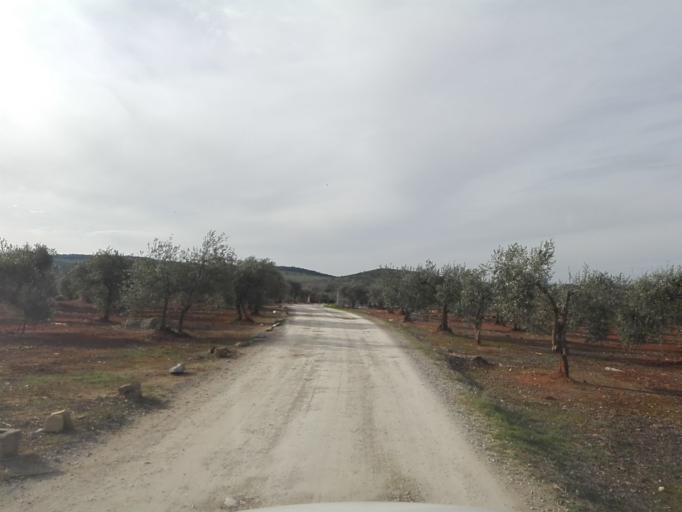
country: ES
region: Extremadura
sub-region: Provincia de Badajoz
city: Llerena
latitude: 38.2258
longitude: -6.0322
